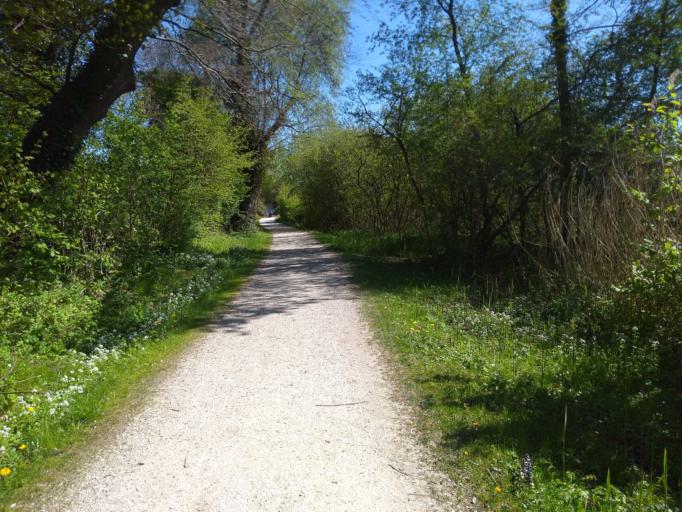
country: DE
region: Bavaria
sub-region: Upper Bavaria
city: Chiemsee
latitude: 47.8778
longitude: 12.3870
